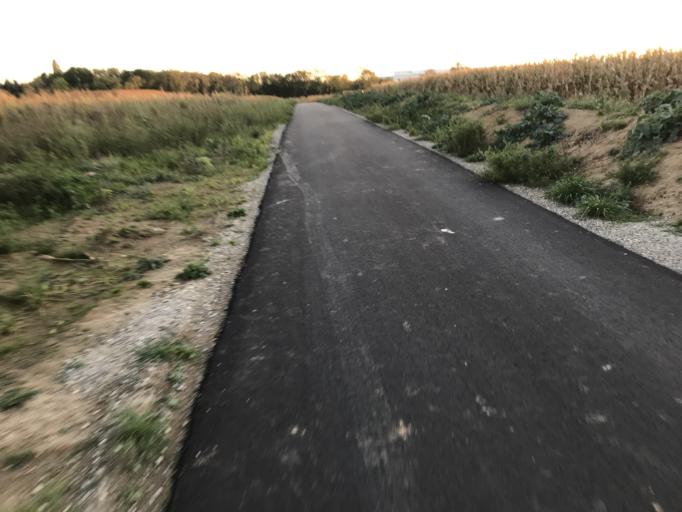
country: FR
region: Ile-de-France
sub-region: Departement de l'Essonne
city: Saclay
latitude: 48.7179
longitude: 2.1803
